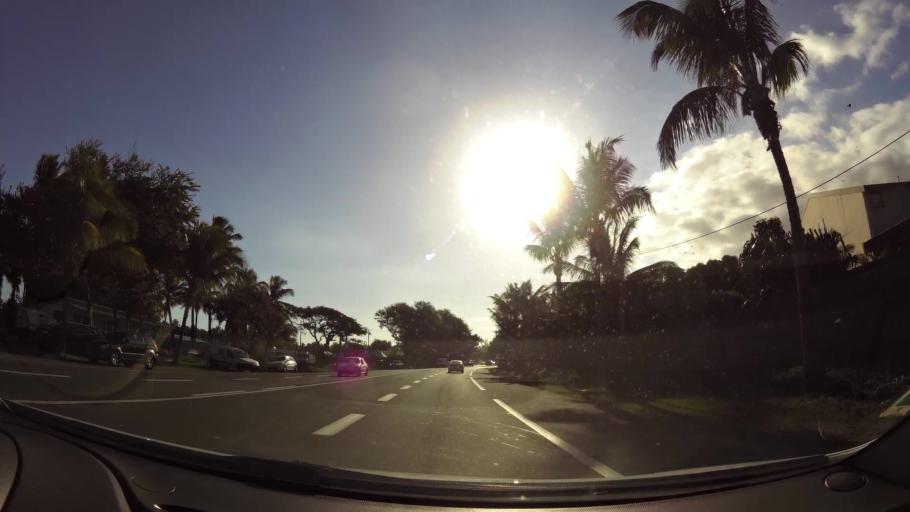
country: RE
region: Reunion
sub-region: Reunion
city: Saint-Louis
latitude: -21.2803
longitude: 55.3756
